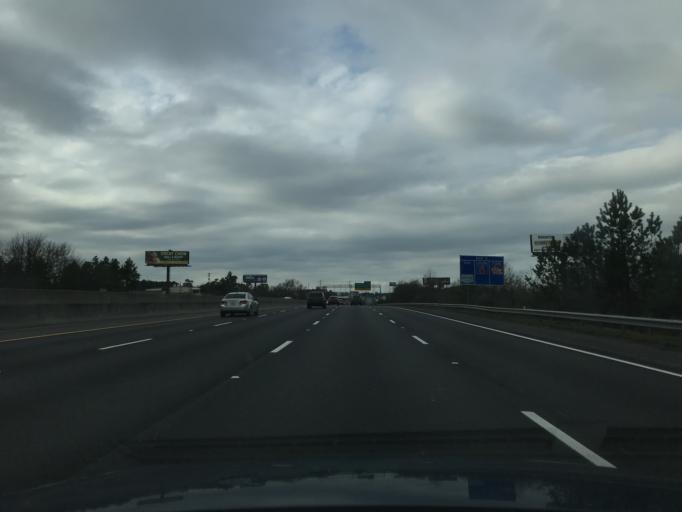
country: US
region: Georgia
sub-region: Columbia County
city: Martinez
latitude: 33.4565
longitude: -82.0763
